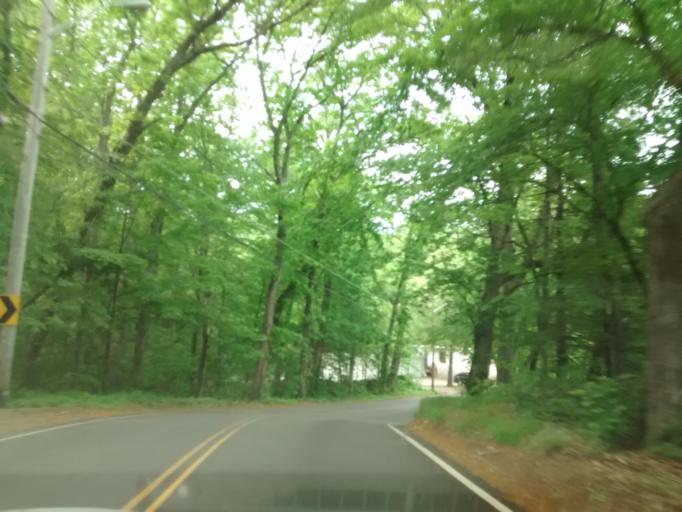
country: US
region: Massachusetts
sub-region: Worcester County
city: Whitinsville
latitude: 42.1021
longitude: -71.6601
